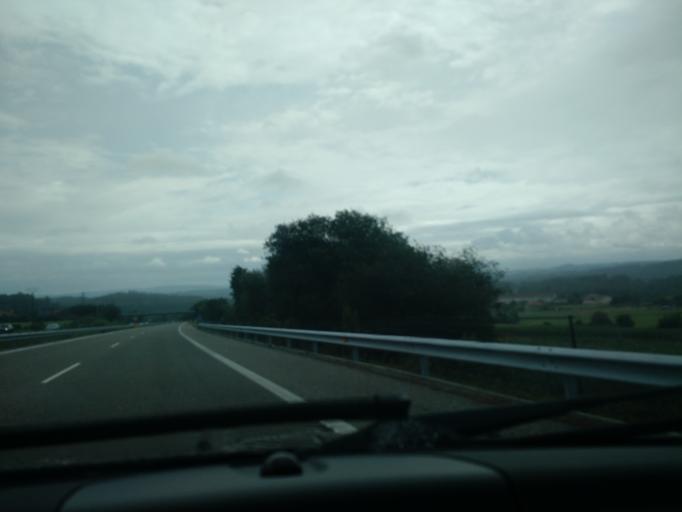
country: ES
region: Galicia
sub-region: Provincia da Coruna
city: Abegondo
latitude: 43.2028
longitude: -8.2934
